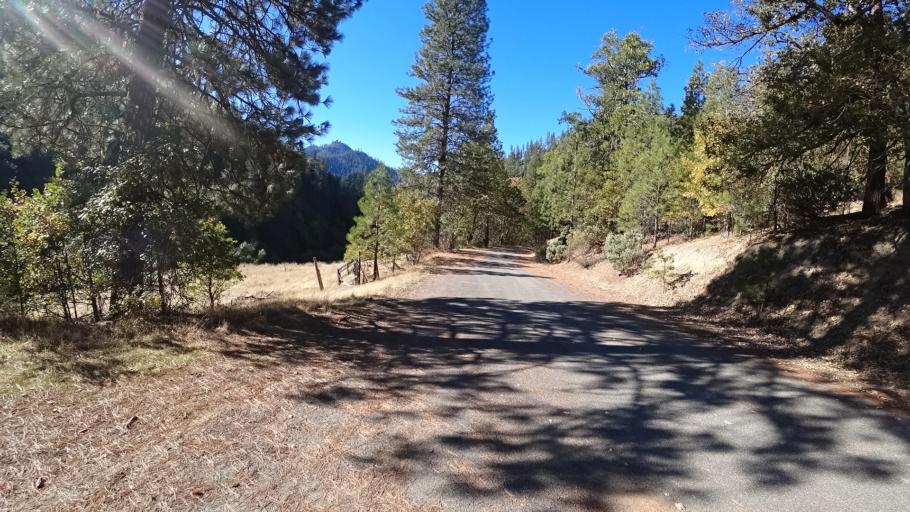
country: US
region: California
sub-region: Trinity County
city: Weaverville
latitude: 41.1529
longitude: -123.1310
